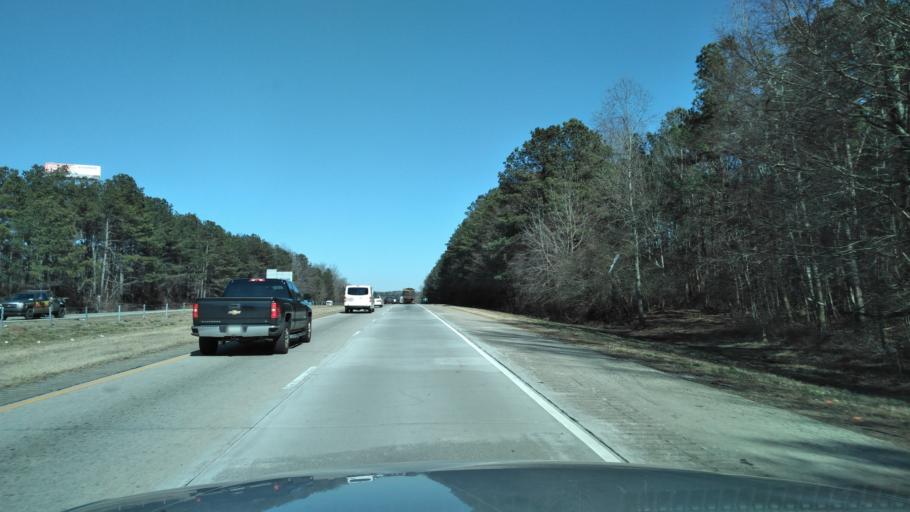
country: US
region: Georgia
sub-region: Hall County
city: Flowery Branch
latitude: 34.1459
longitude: -83.9429
